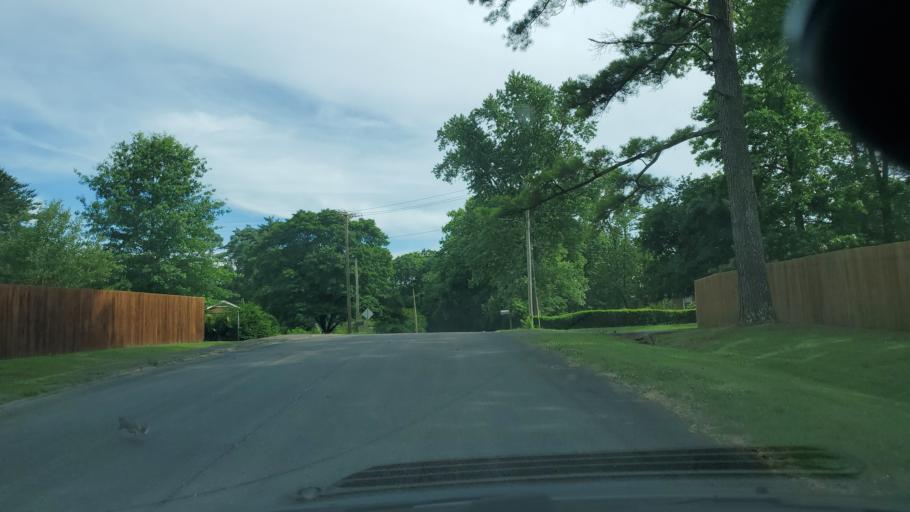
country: US
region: Tennessee
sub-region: Davidson County
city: Lakewood
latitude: 36.2009
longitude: -86.6811
